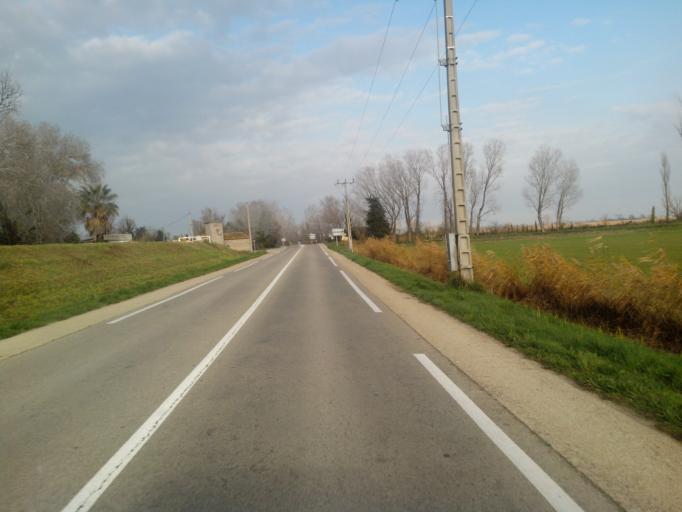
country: FR
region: Languedoc-Roussillon
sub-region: Departement du Gard
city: Saint-Gilles
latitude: 43.6063
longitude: 4.4763
